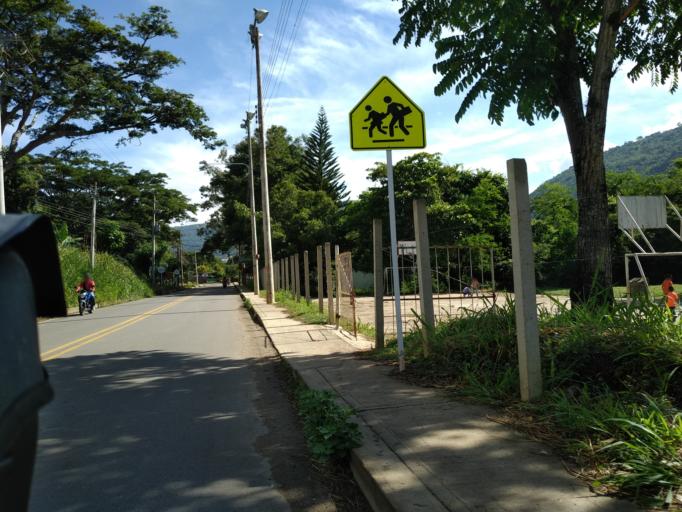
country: CO
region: Santander
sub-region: San Gil
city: San Gil
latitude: 6.5368
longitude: -73.1263
